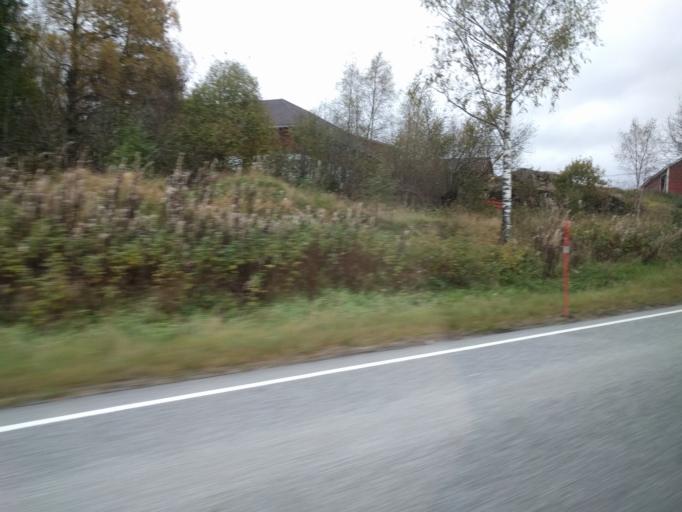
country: NO
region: Aust-Agder
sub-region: Evje og Hornnes
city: Evje
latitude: 58.5609
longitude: 7.7706
